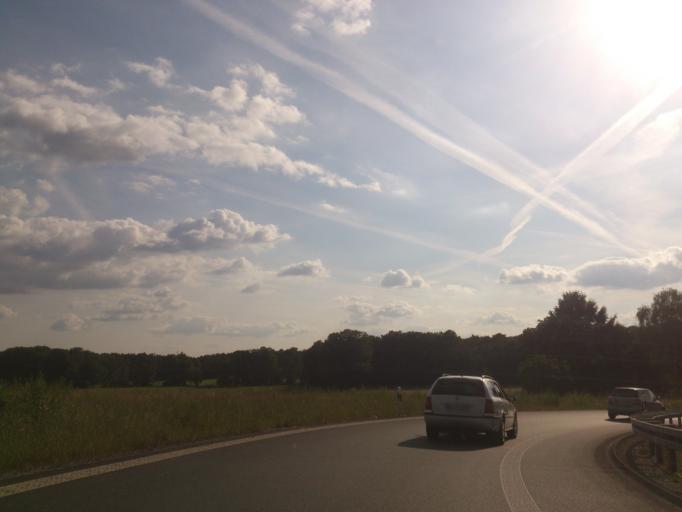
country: DE
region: North Rhine-Westphalia
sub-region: Regierungsbezirk Detmold
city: Bielefeld
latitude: 51.9722
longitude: 8.4792
